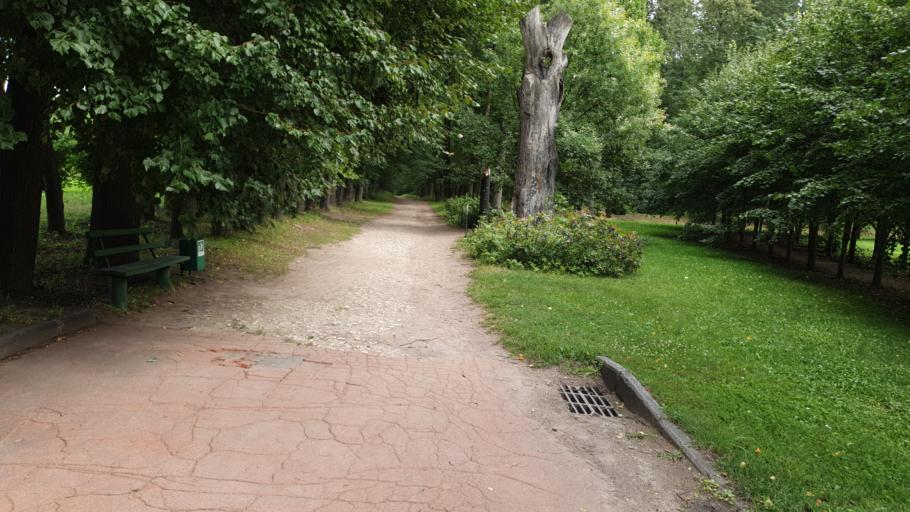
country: RU
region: Moskovskaya
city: Gorki-Leninskiye
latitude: 55.5048
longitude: 37.7654
